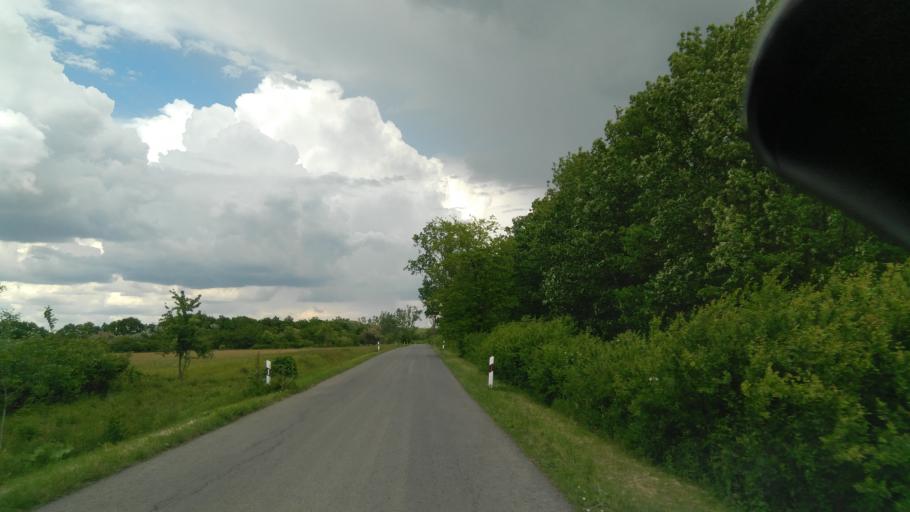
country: HU
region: Bekes
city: Bucsa
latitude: 47.1562
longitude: 21.0755
